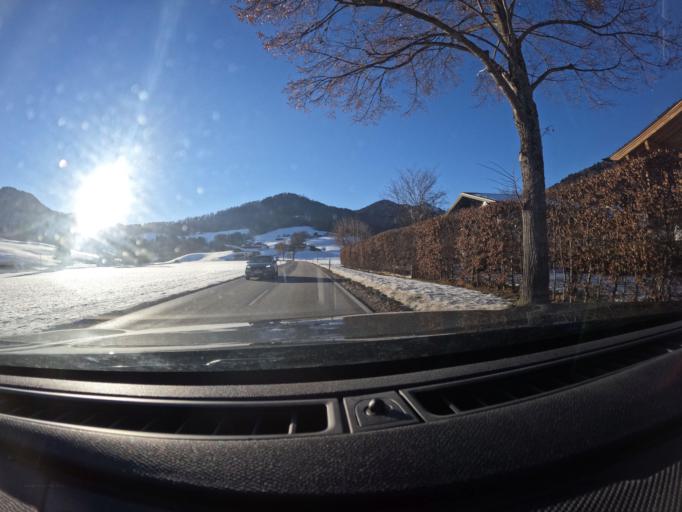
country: DE
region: Bavaria
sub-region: Upper Bavaria
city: Ruhpolding
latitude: 47.7583
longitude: 12.6359
